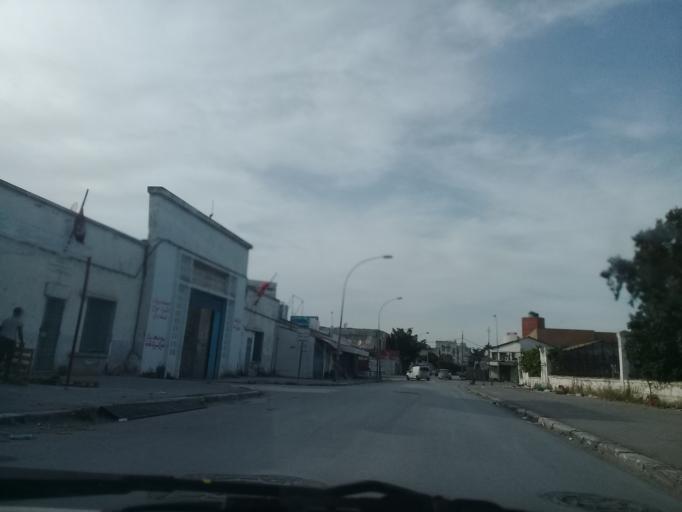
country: TN
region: Tunis
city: Tunis
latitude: 36.7921
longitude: 10.1876
